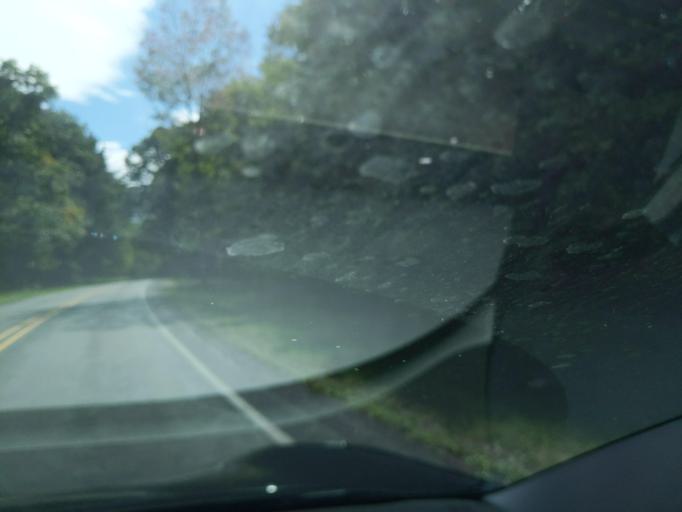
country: US
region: Michigan
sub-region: Antrim County
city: Bellaire
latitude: 45.0092
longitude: -85.2923
